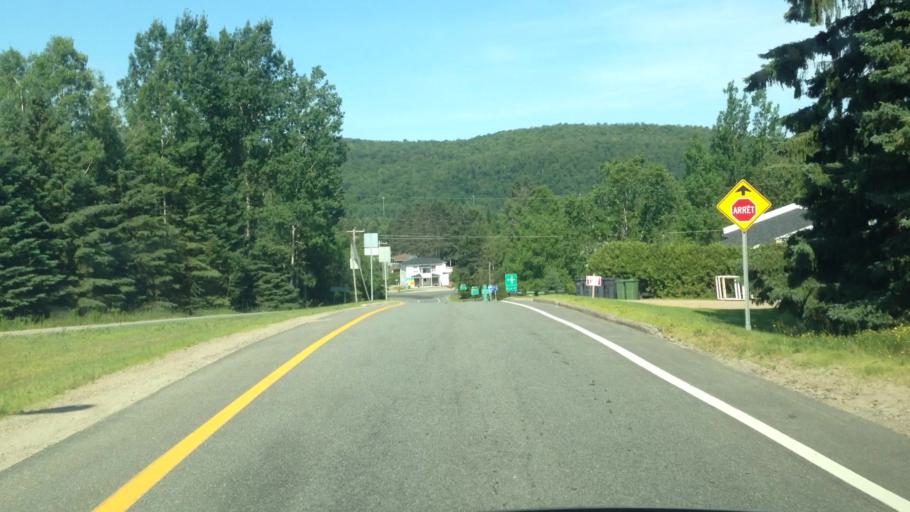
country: CA
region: Quebec
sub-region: Laurentides
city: Mont-Tremblant
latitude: 46.1145
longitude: -74.5932
